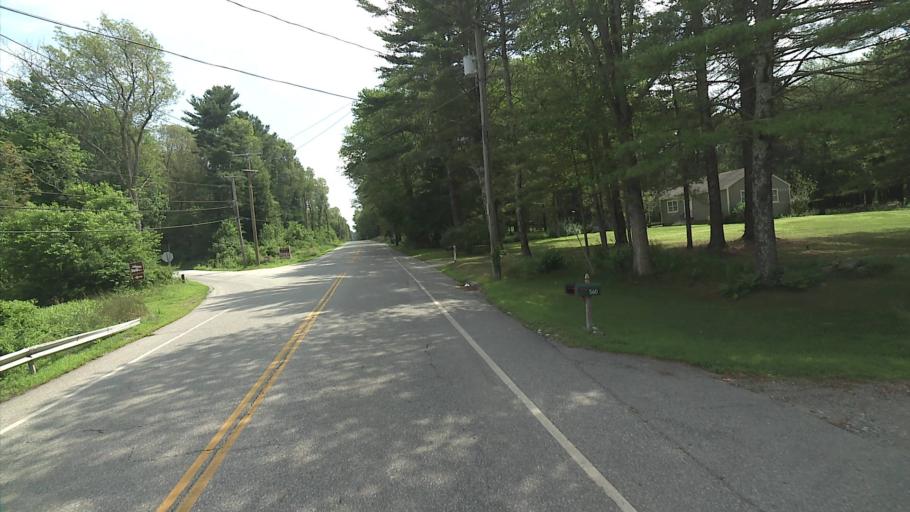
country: US
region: Rhode Island
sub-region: Washington County
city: Hopkinton
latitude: 41.5742
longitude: -71.8217
